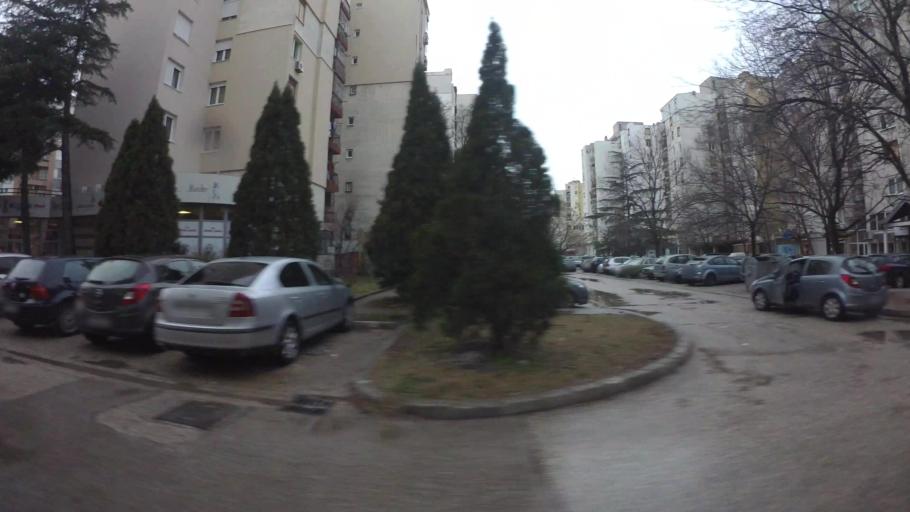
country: BA
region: Federation of Bosnia and Herzegovina
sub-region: Hercegovacko-Bosanski Kanton
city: Mostar
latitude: 43.3515
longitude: 17.8048
